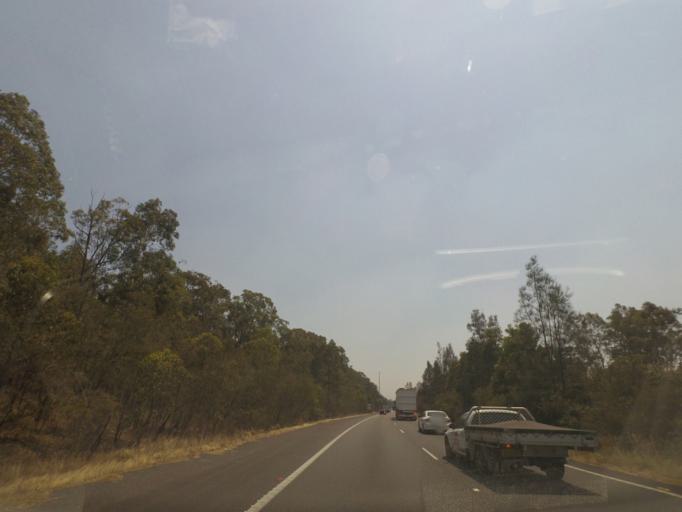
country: AU
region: New South Wales
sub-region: Newcastle
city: Beresfield
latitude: -32.8263
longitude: 151.6330
